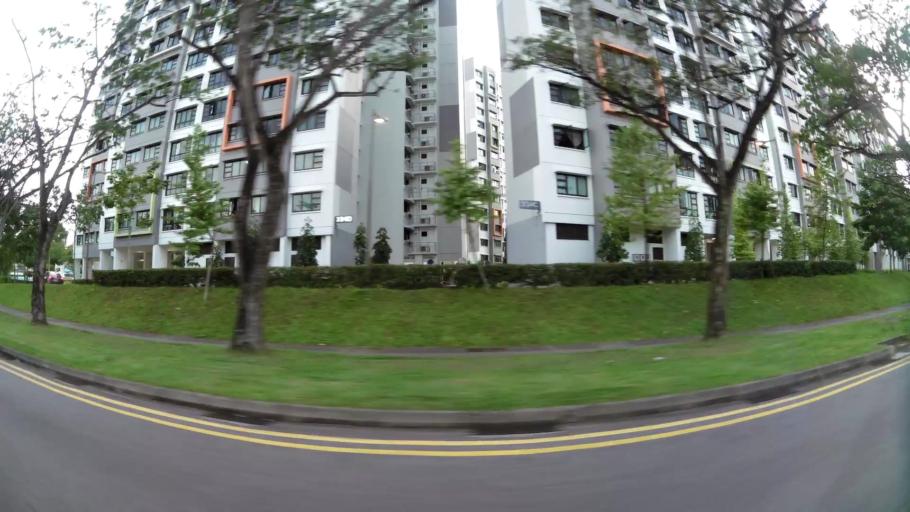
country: MY
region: Johor
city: Kampung Pasir Gudang Baru
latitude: 1.4329
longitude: 103.8465
